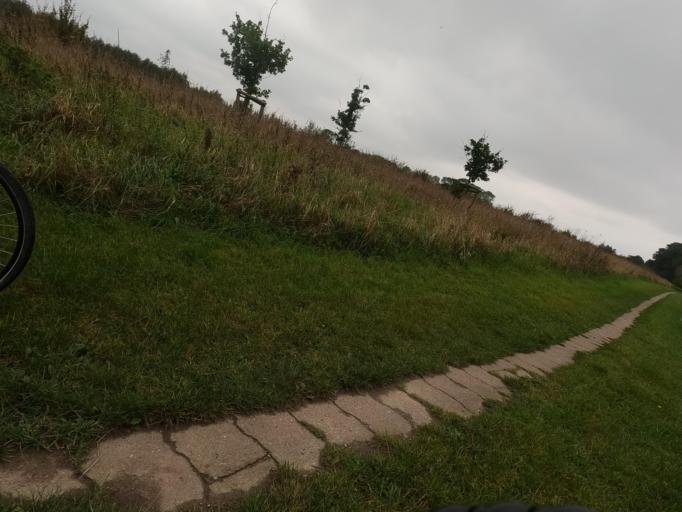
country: DE
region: Schleswig-Holstein
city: Heiligenhafen
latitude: 54.3593
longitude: 10.9967
